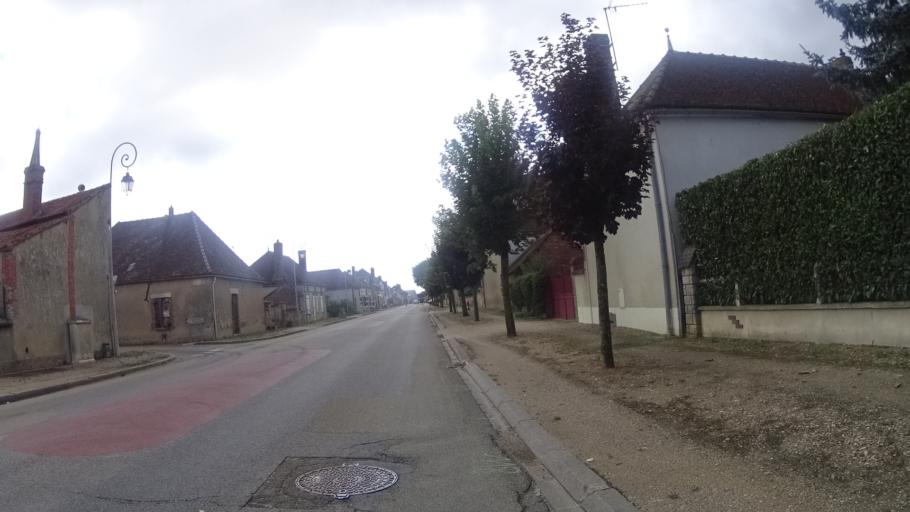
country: FR
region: Bourgogne
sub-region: Departement de l'Yonne
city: Neuvy-Sautour
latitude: 47.9956
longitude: 3.7776
